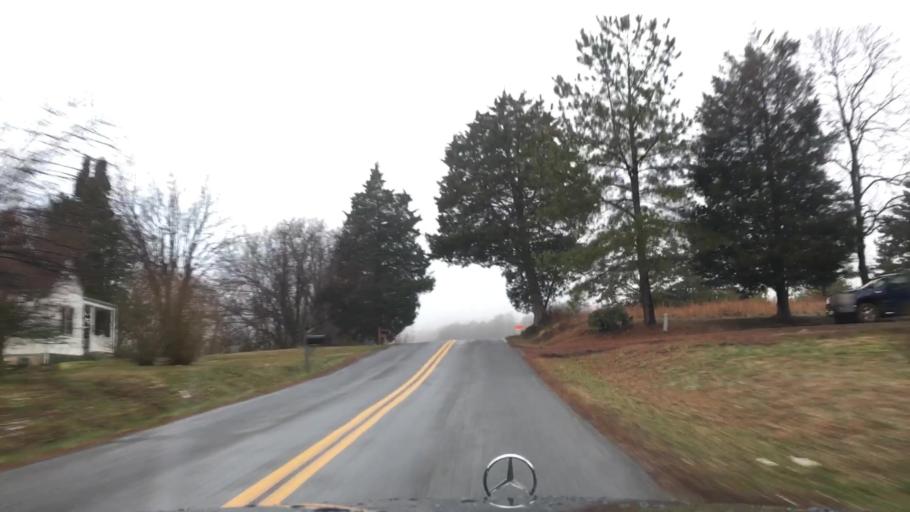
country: US
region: Virginia
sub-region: Pittsylvania County
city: Hurt
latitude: 37.1142
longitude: -79.3233
